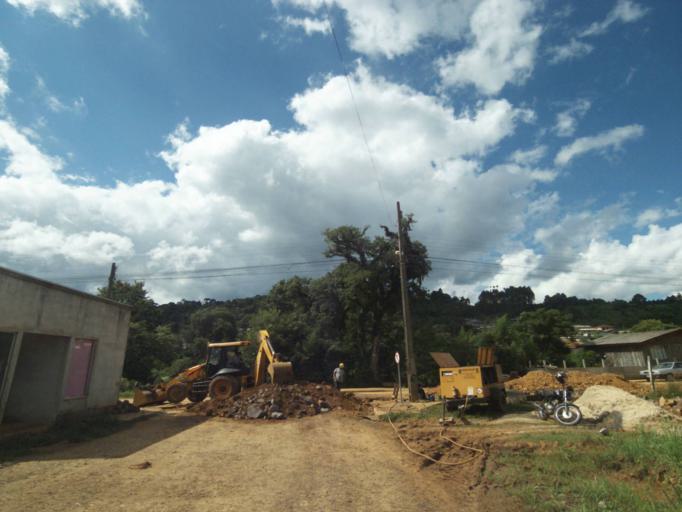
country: BR
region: Parana
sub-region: Uniao Da Vitoria
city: Uniao da Vitoria
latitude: -26.1505
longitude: -51.5418
